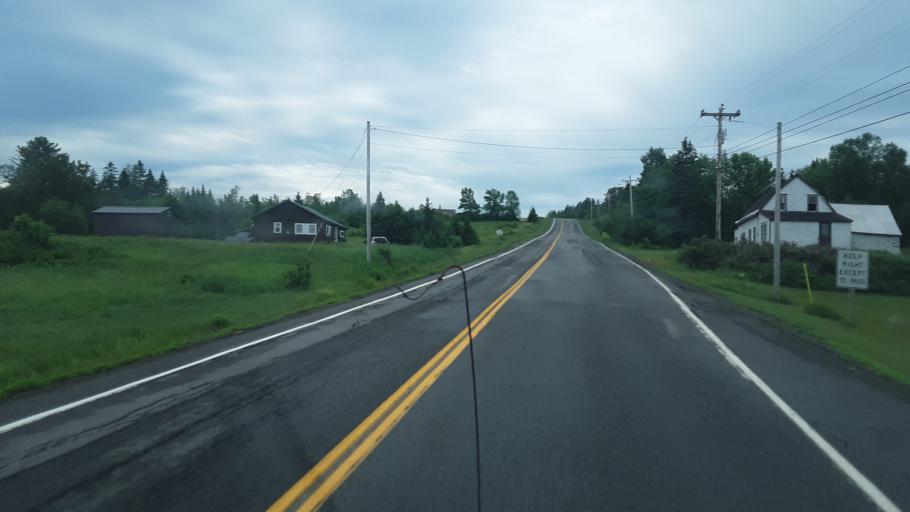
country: US
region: Maine
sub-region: Penobscot County
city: Patten
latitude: 46.0513
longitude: -68.4424
